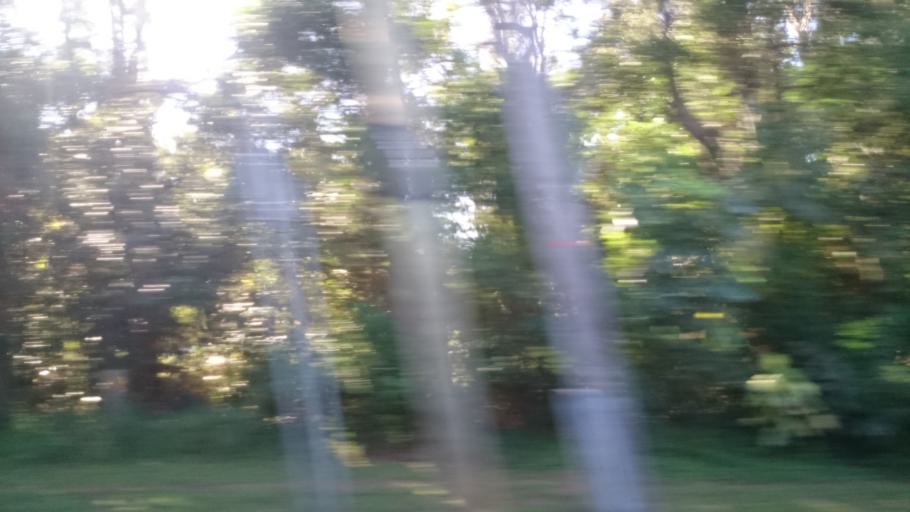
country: AU
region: Queensland
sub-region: Brisbane
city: Manly West
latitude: -27.4677
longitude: 153.1874
